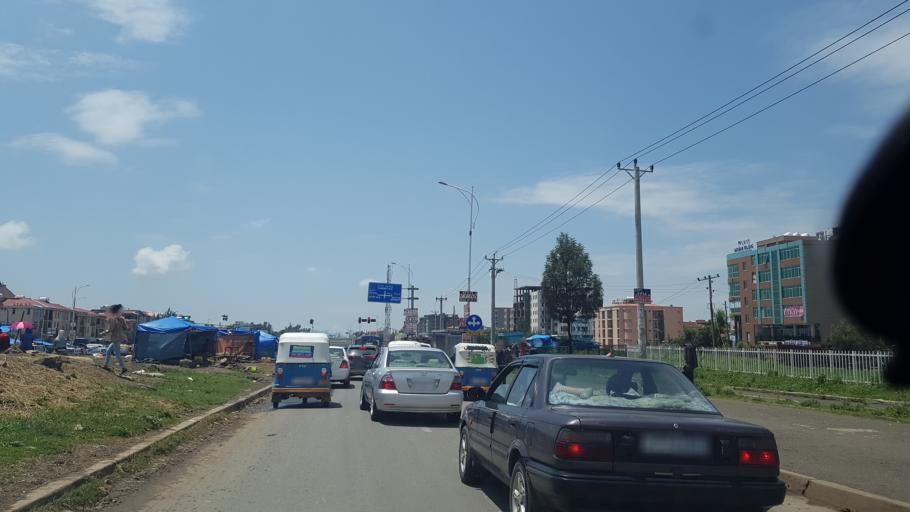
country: ET
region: Adis Abeba
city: Addis Ababa
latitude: 9.0115
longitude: 38.8520
